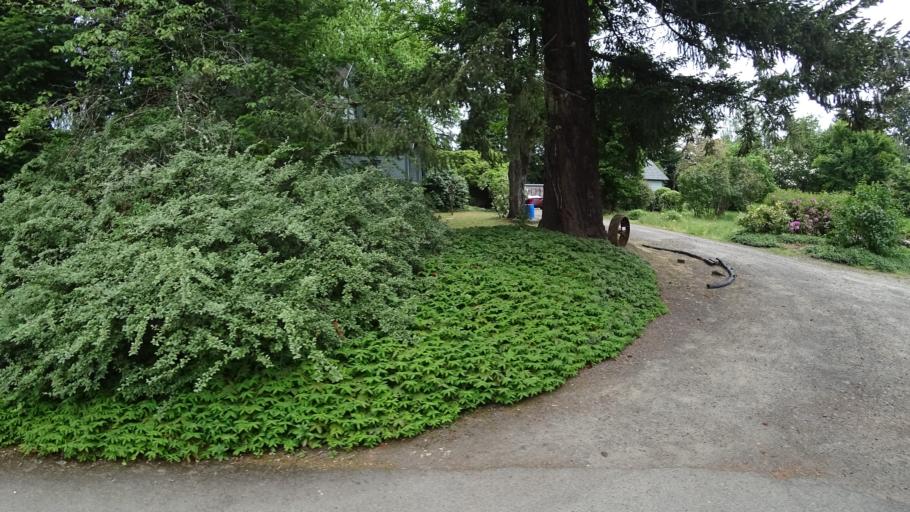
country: US
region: Oregon
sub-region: Washington County
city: Raleigh Hills
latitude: 45.4806
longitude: -122.7472
